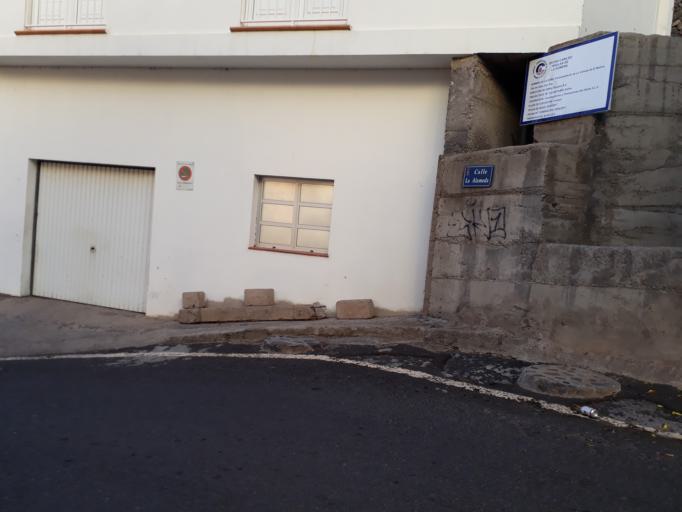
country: ES
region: Canary Islands
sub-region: Provincia de Santa Cruz de Tenerife
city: Alajero
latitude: 28.0966
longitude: -17.3348
